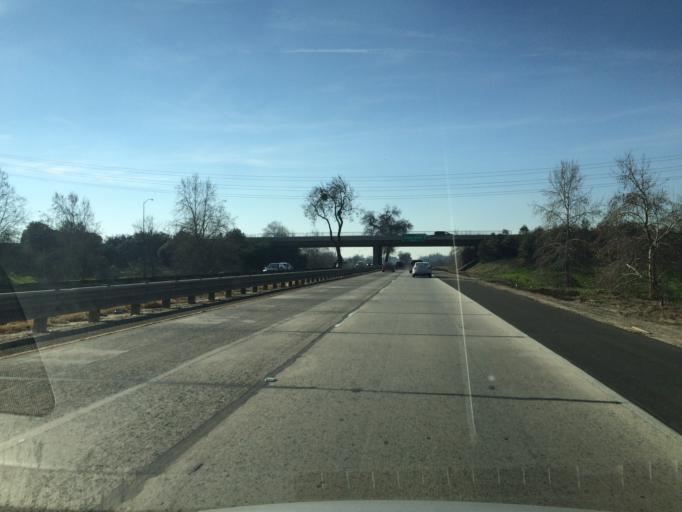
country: US
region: California
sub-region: Tulare County
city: Goshen
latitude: 36.3273
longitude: -119.3658
